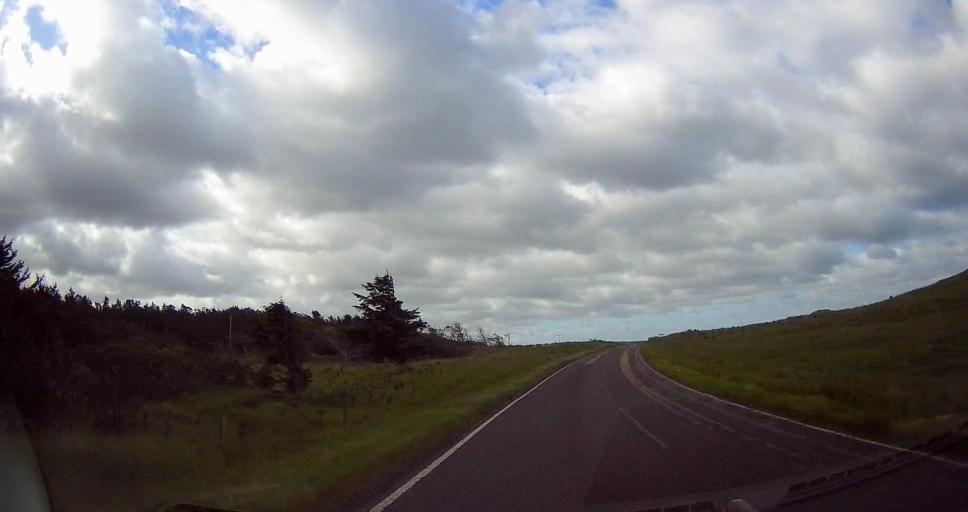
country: GB
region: Scotland
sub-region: Highland
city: Thurso
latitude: 58.6118
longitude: -3.3432
